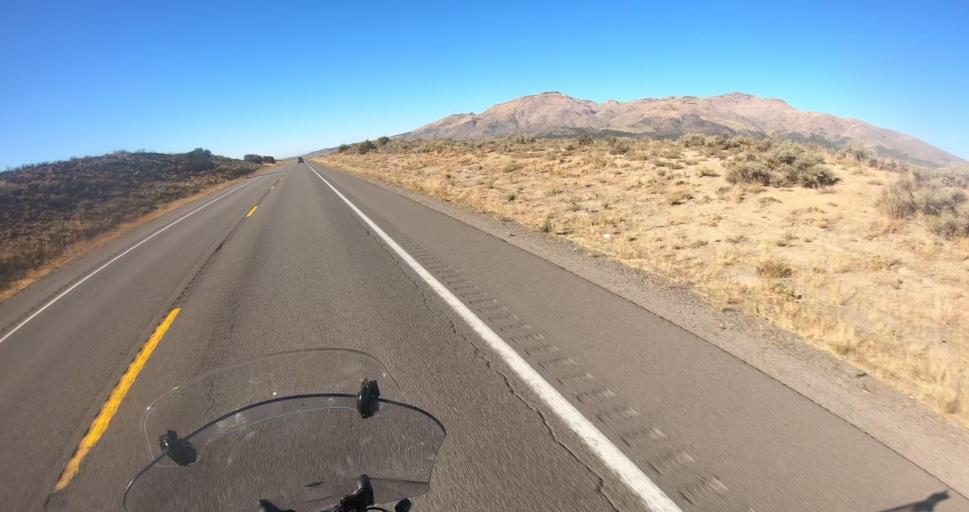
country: US
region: Nevada
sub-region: Washoe County
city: Cold Springs
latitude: 39.9423
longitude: -120.0229
